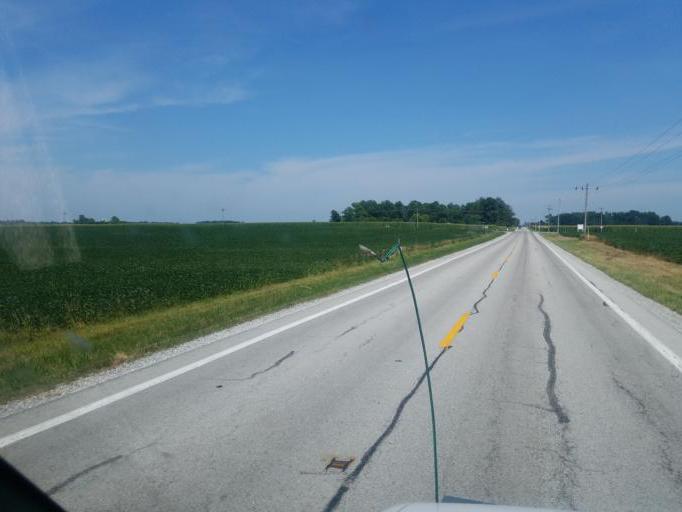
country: US
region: Ohio
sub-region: Shelby County
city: Botkins
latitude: 40.4964
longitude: -84.2617
